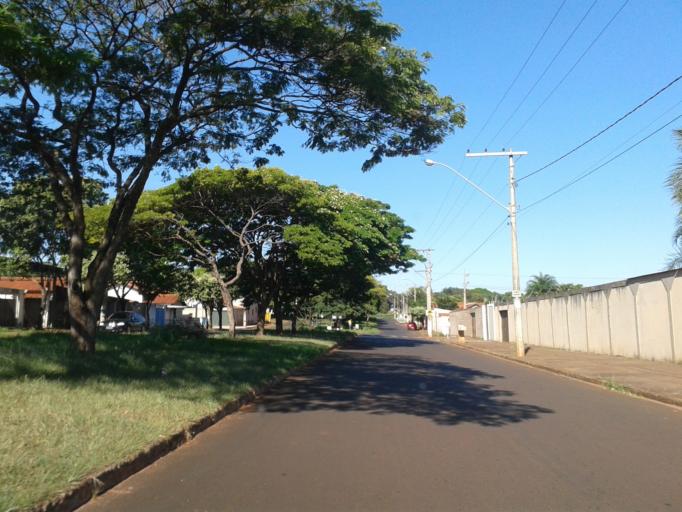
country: BR
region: Minas Gerais
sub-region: Ituiutaba
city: Ituiutaba
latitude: -18.9808
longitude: -49.4877
